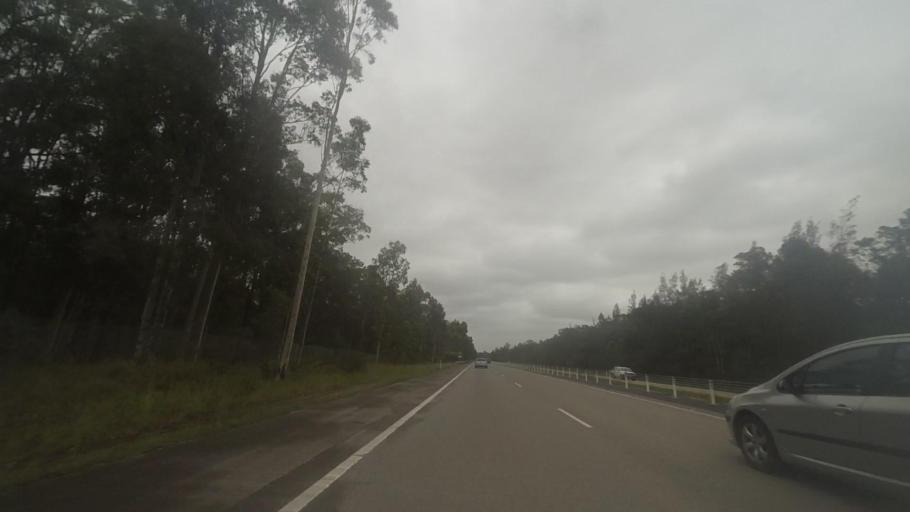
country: AU
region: New South Wales
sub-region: Port Stephens Shire
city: Medowie
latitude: -32.6978
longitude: 151.8059
